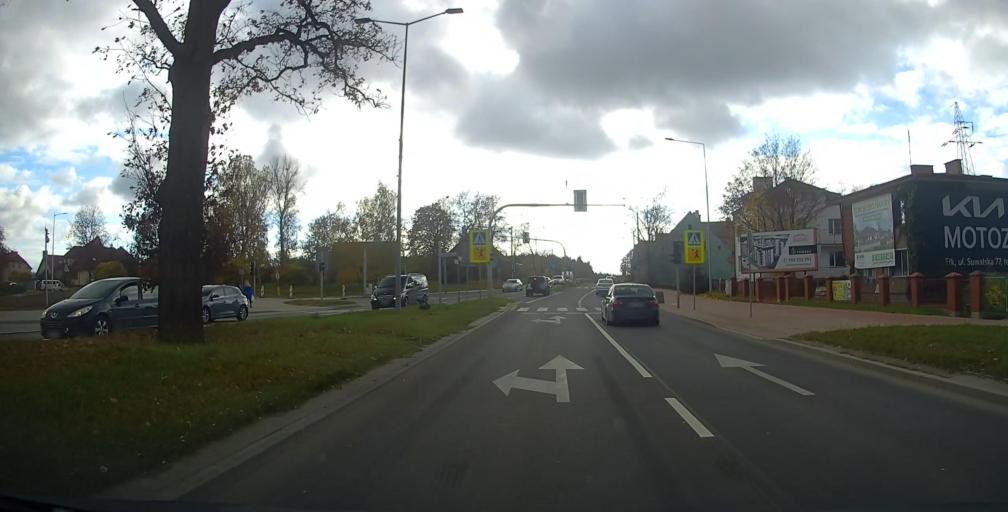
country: PL
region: Warmian-Masurian Voivodeship
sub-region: Powiat elcki
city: Elk
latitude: 53.8055
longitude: 22.3674
